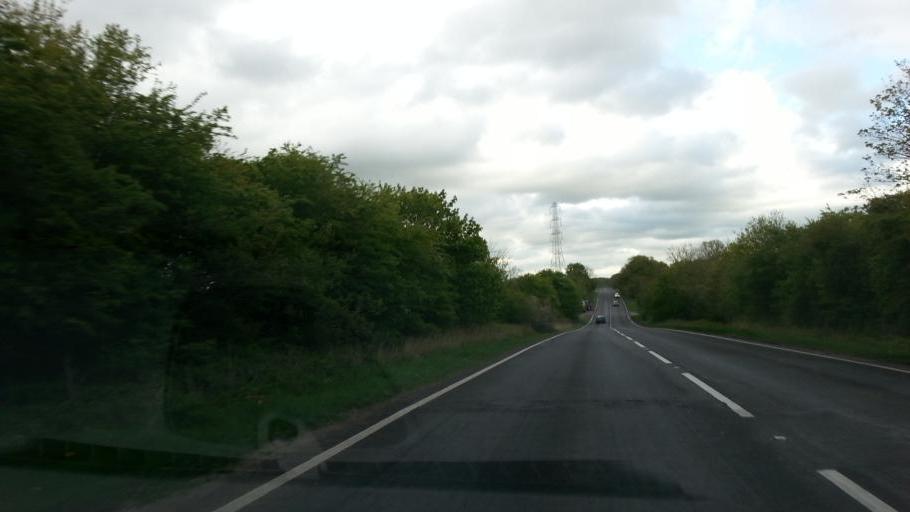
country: GB
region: England
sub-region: Nottinghamshire
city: Farndon
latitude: 53.1254
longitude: -0.8793
